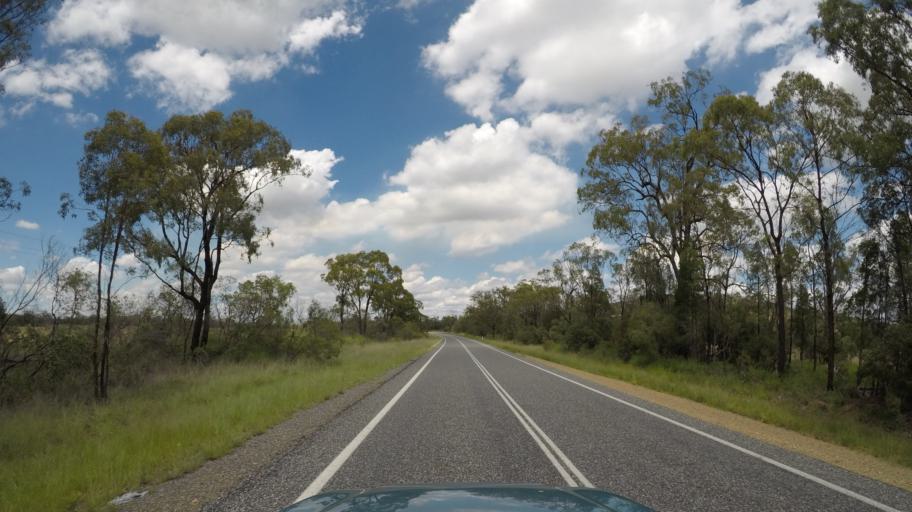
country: AU
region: Queensland
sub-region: Toowoomba
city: Oakey
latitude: -27.9181
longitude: 151.1760
